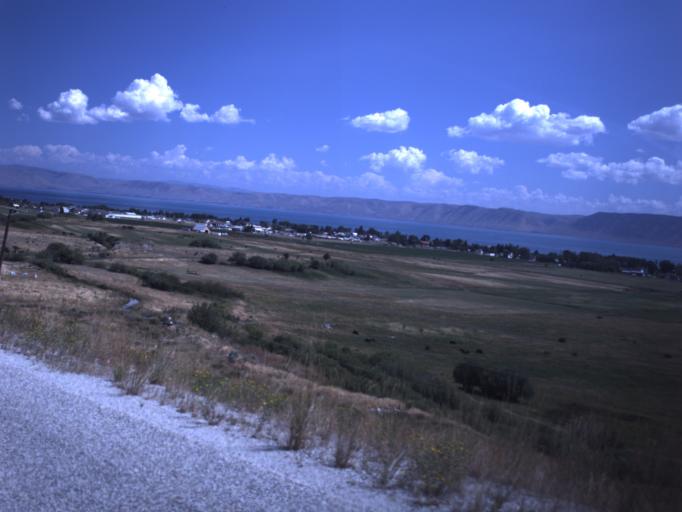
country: US
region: Idaho
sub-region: Bear Lake County
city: Paris
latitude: 41.9383
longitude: -111.4108
